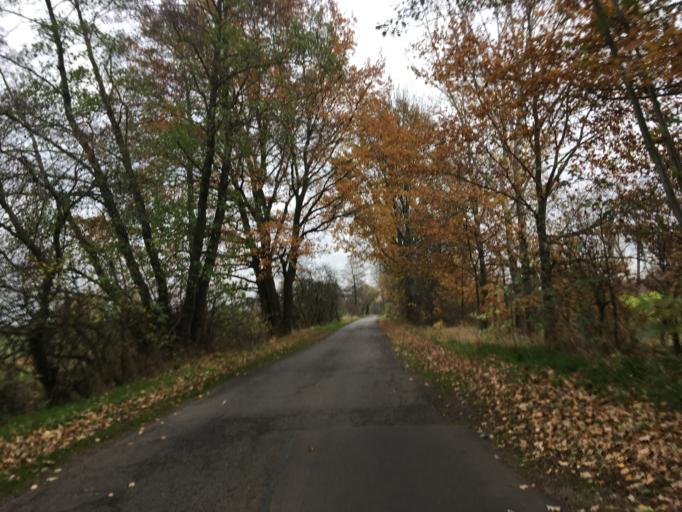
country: DE
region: Brandenburg
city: Drehnow
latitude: 51.8607
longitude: 14.3869
